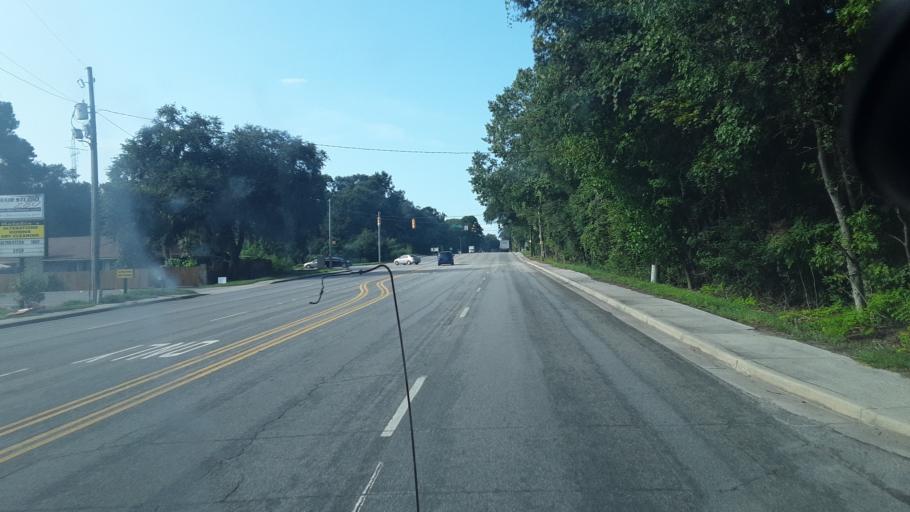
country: US
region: South Carolina
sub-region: Beaufort County
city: Shell Point
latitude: 32.4097
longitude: -80.7332
